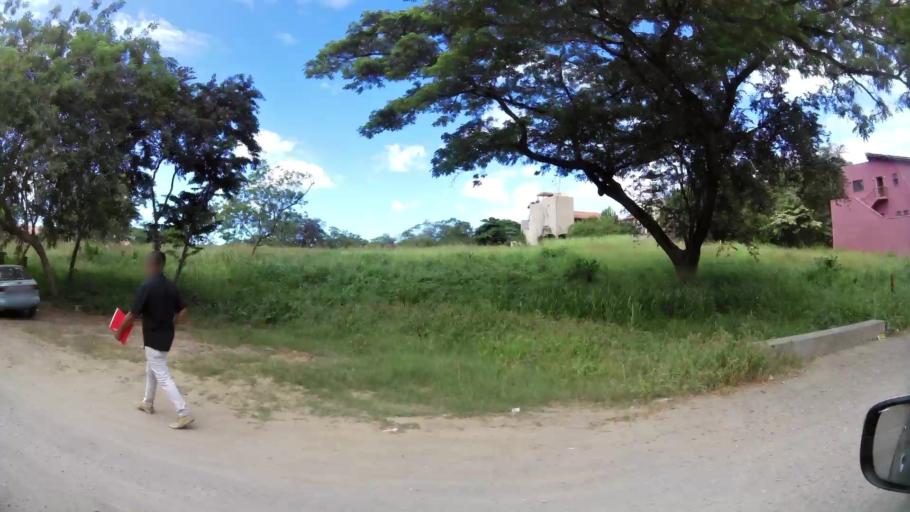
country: CR
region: Guanacaste
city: Santa Cruz
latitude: 10.2876
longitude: -85.8489
